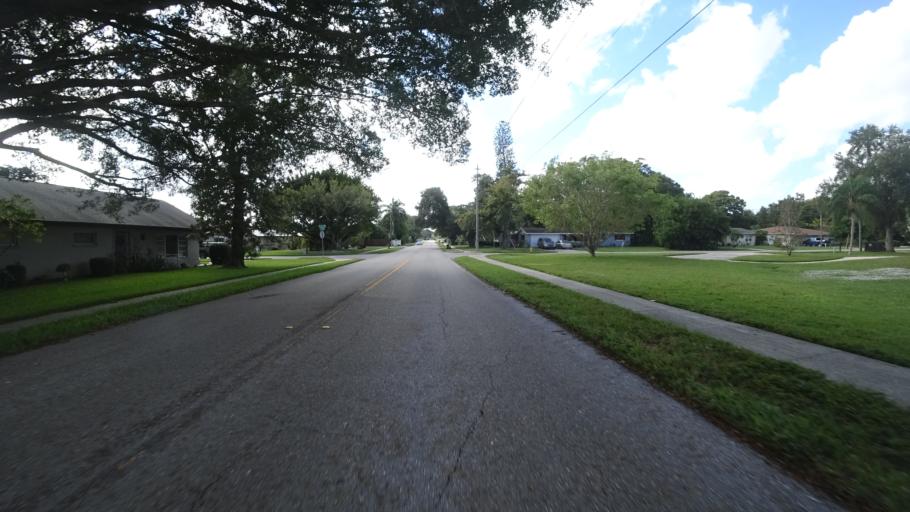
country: US
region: Florida
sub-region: Manatee County
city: West Bradenton
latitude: 27.5075
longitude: -82.6324
